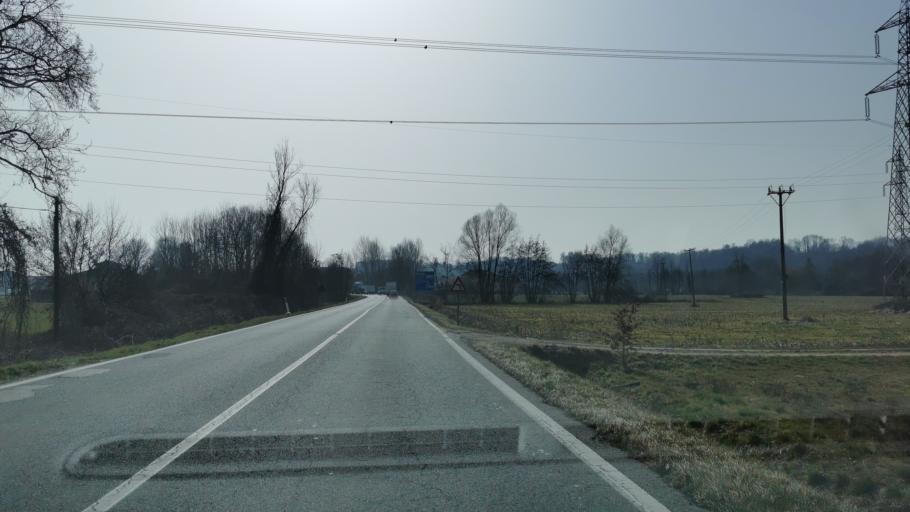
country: IT
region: Piedmont
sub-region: Provincia di Torino
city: Volpiano
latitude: 45.2131
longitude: 7.7733
